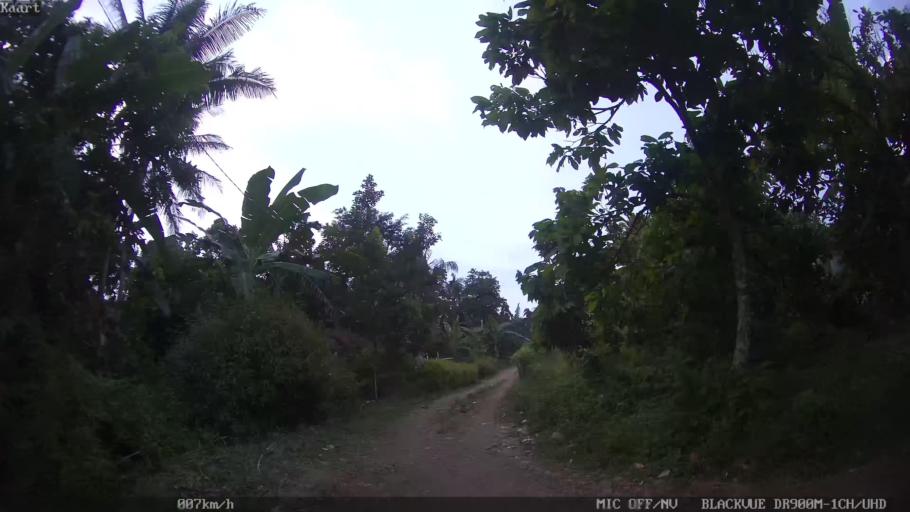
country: ID
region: Lampung
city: Kedaton
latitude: -5.3929
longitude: 105.1980
